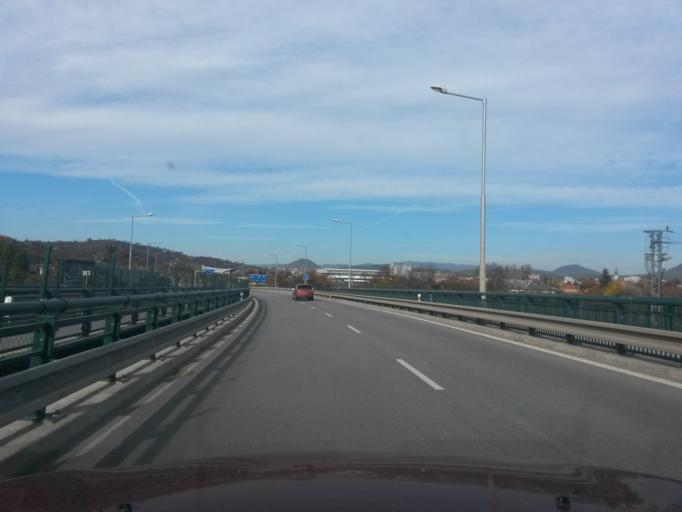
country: SK
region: Presovsky
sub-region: Okres Presov
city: Presov
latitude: 48.9800
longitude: 21.2397
